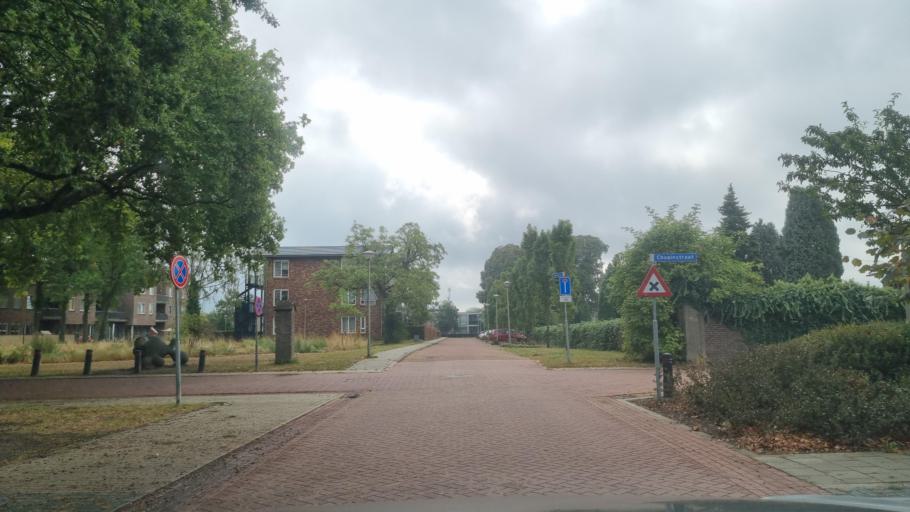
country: NL
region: Gelderland
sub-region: Gemeente Zevenaar
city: Zevenaar
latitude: 51.8622
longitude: 6.0446
